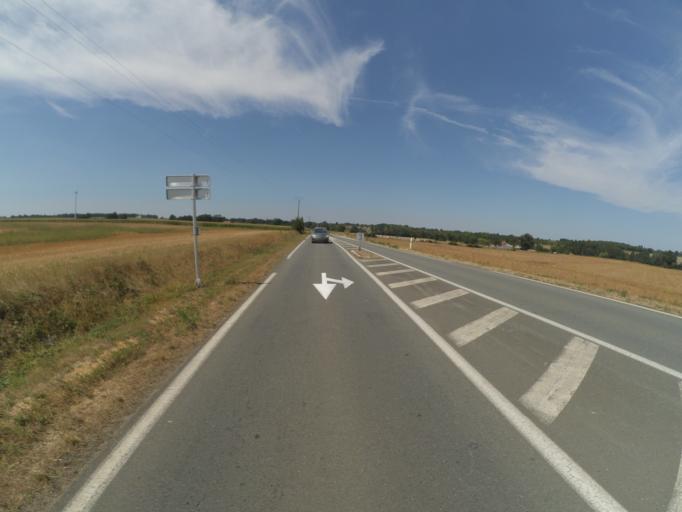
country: FR
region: Poitou-Charentes
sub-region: Departement de la Vienne
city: Saint-Maurice-la-Clouere
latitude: 46.3546
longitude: 0.4453
